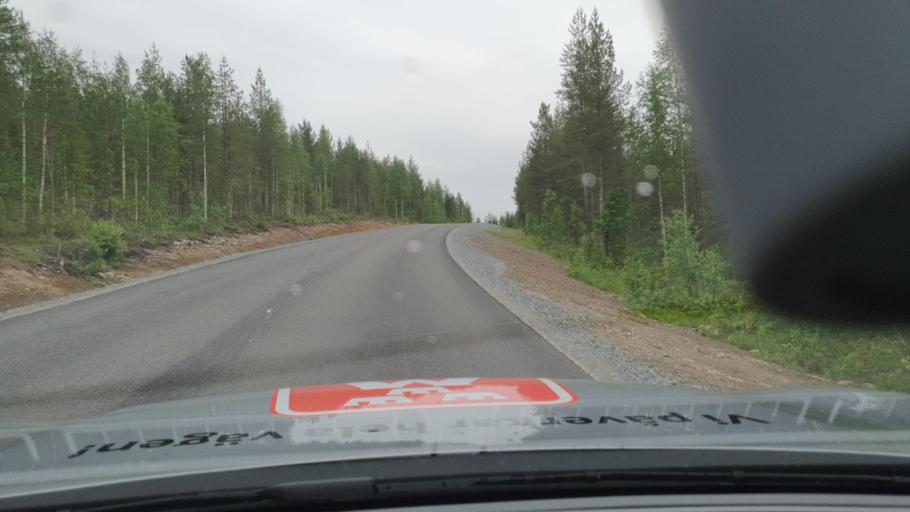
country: SE
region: Norrbotten
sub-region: Overtornea Kommun
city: OEvertornea
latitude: 66.5999
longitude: 23.3058
